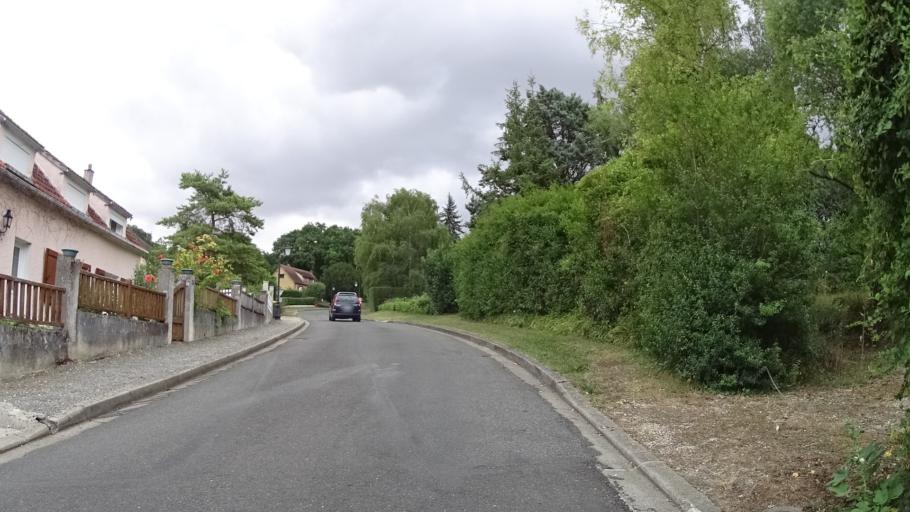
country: FR
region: Centre
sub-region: Departement du Loiret
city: Amilly
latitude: 47.9527
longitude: 2.7884
